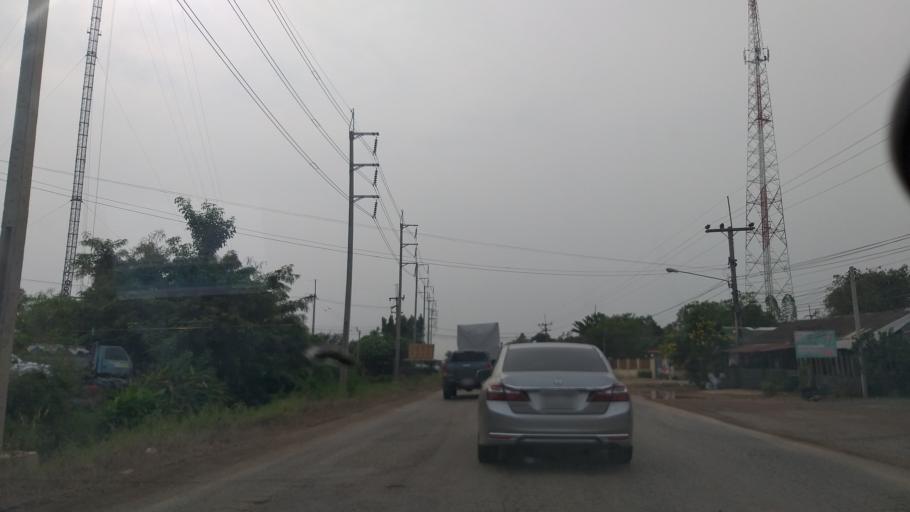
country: TH
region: Chachoengsao
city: Plaeng Yao
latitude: 13.5976
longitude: 101.1846
